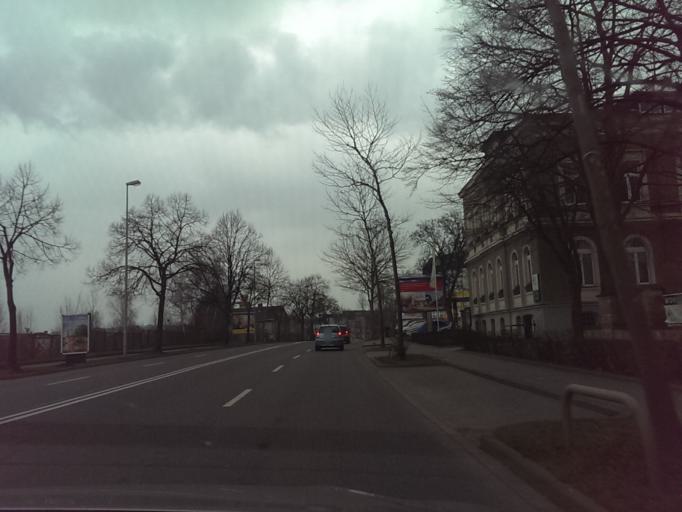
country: DE
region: Saxony
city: Chemnitz
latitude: 50.8411
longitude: 12.9342
